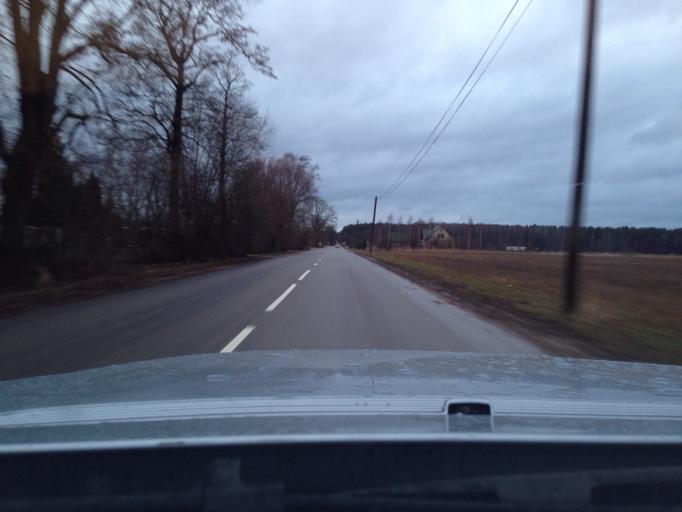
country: LV
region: Marupe
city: Marupe
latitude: 56.8795
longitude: 23.9804
